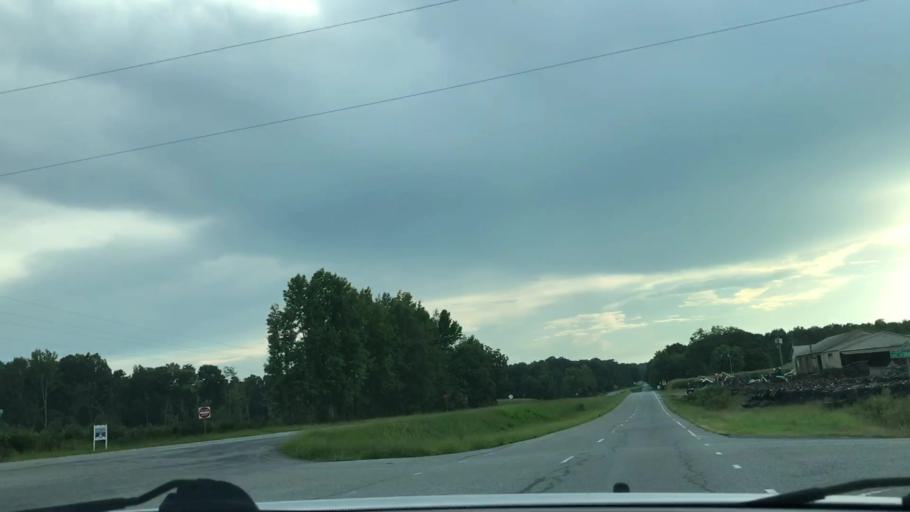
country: US
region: North Carolina
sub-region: Davidson County
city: Denton
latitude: 35.5878
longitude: -80.0522
